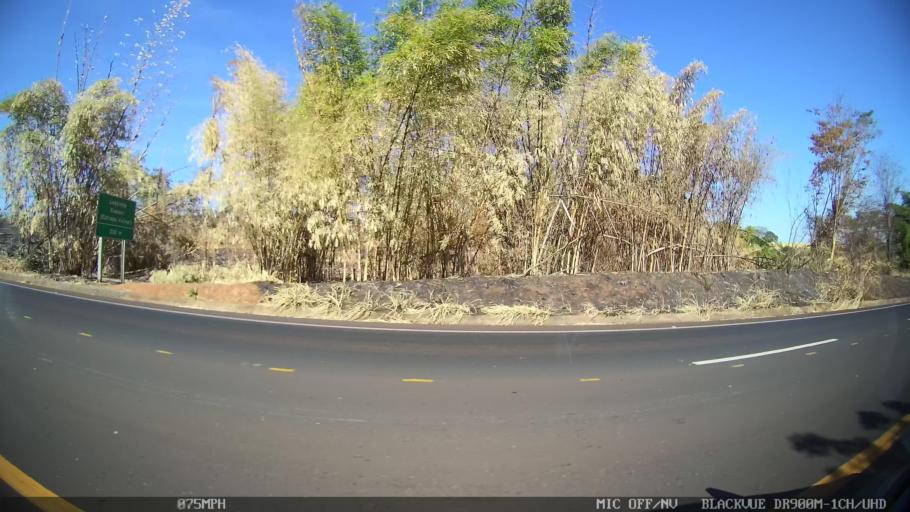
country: BR
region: Sao Paulo
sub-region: Barretos
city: Barretos
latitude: -20.6129
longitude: -48.7554
